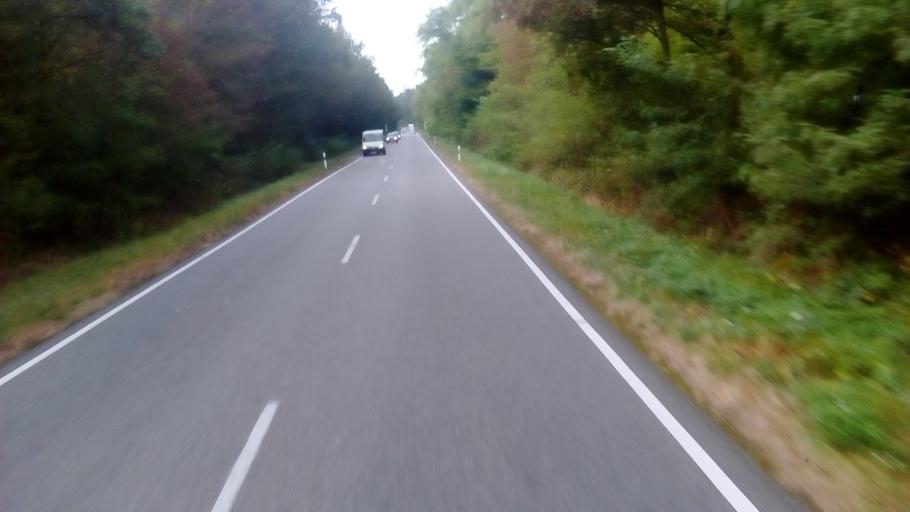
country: DE
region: Rheinland-Pfalz
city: Berg
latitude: 49.0051
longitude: 8.1831
